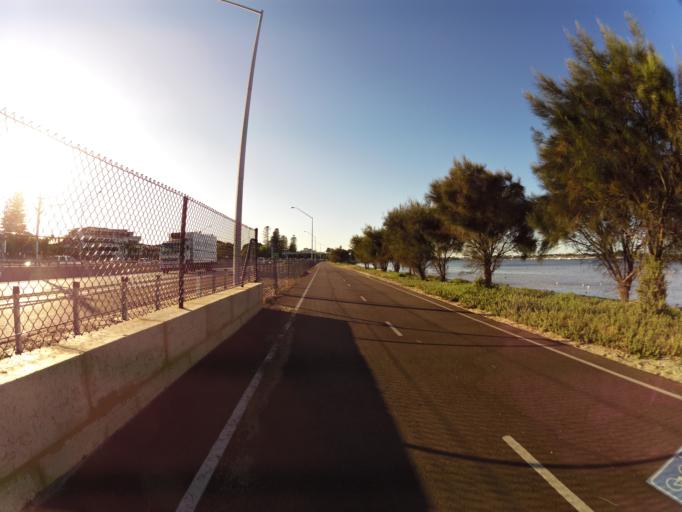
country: AU
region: Western Australia
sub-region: South Perth
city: Como
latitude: -31.9886
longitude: 115.8532
